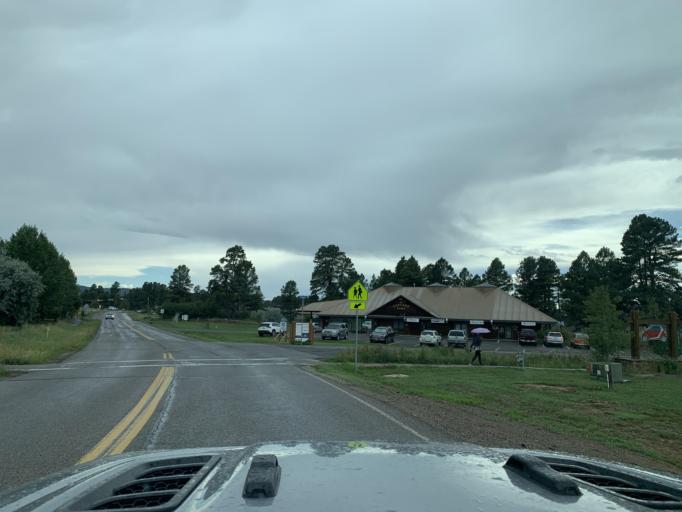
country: US
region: Colorado
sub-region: Archuleta County
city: Pagosa Springs
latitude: 37.2578
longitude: -107.0767
